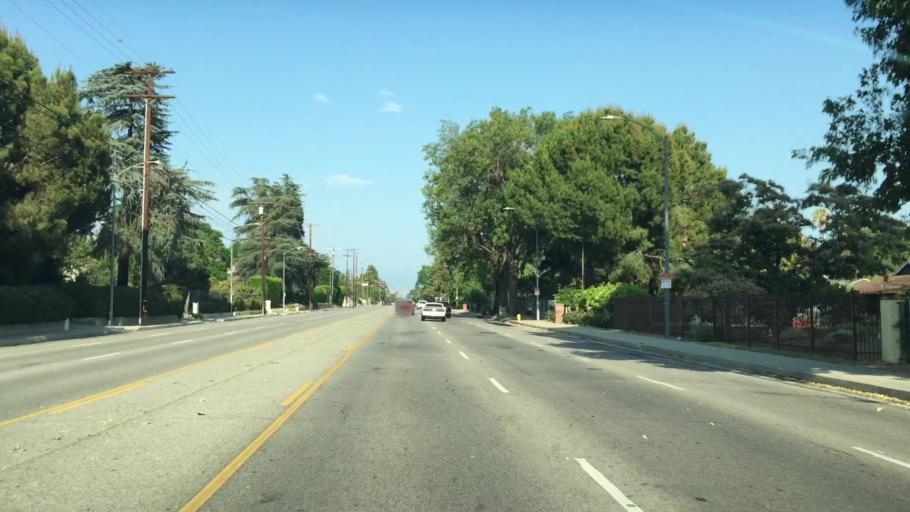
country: US
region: California
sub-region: Los Angeles County
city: Northridge
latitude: 34.2358
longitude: -118.5185
